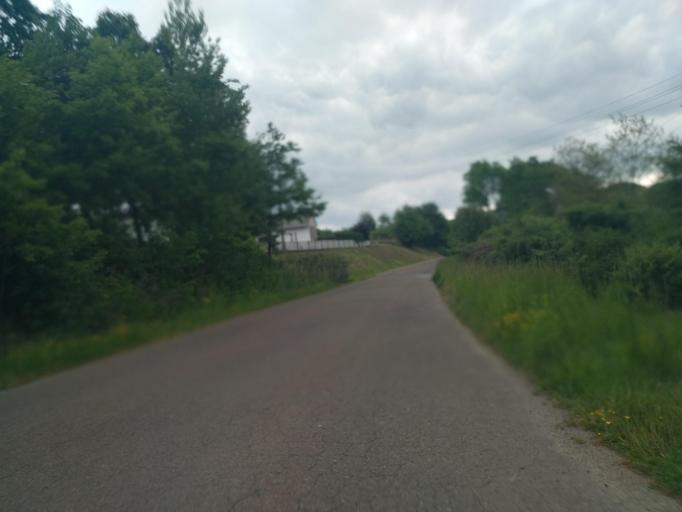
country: PL
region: Subcarpathian Voivodeship
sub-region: Powiat jasielski
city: Tarnowiec
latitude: 49.6794
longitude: 21.5913
